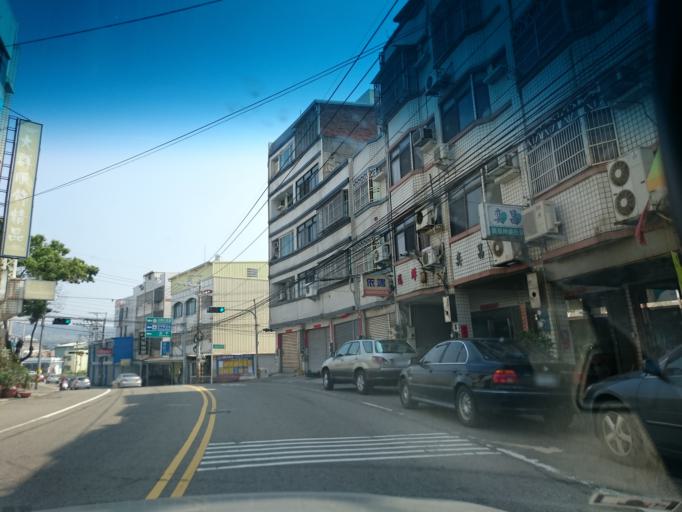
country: TW
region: Taiwan
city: Fengyuan
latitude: 24.2431
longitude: 120.5706
